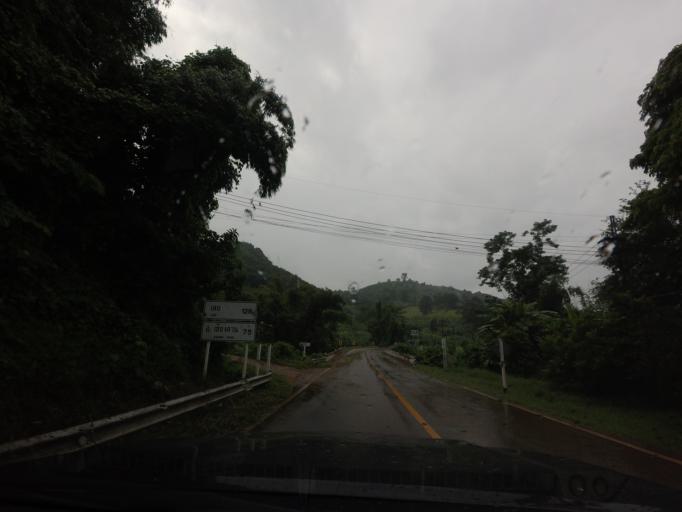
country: TH
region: Nong Khai
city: Sangkhom
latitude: 18.2077
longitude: 102.1037
